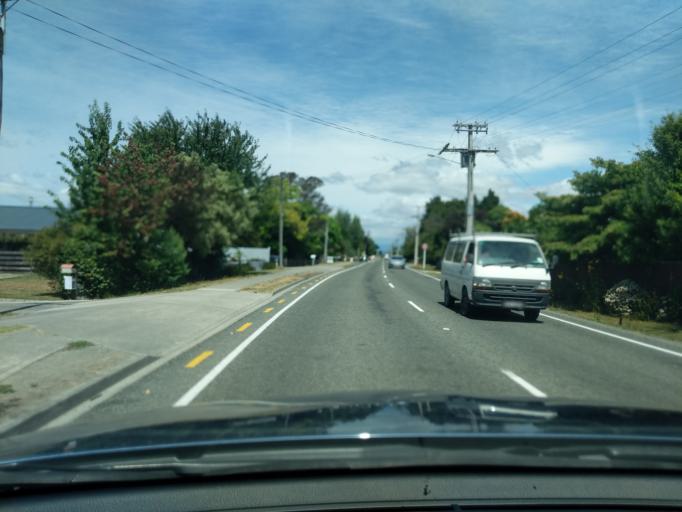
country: NZ
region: Tasman
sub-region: Tasman District
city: Motueka
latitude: -41.0822
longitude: 172.9971
